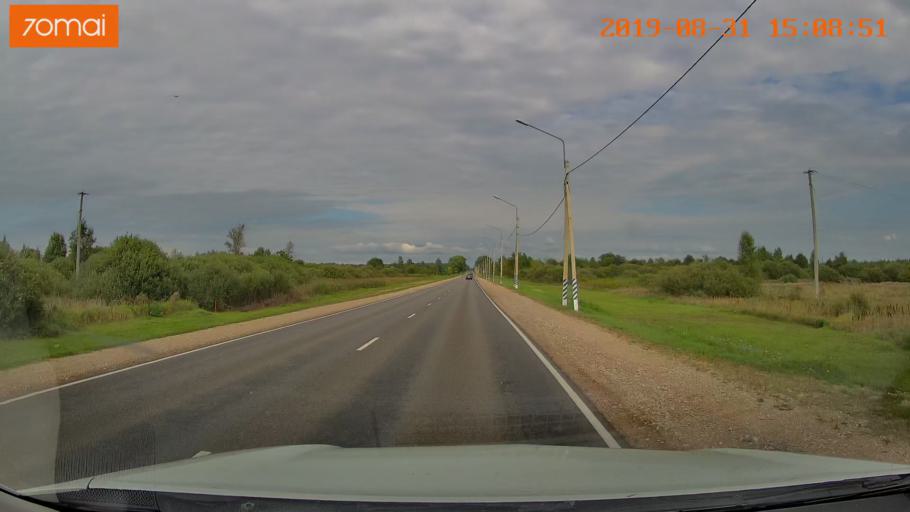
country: RU
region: Kaluga
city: Spas-Demensk
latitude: 54.3957
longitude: 34.1904
